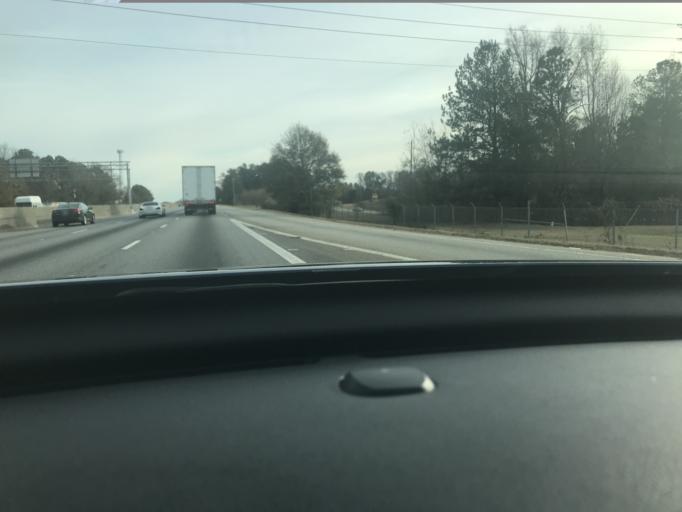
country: US
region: Georgia
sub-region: Rockdale County
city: Lakeview Estates
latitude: 33.6819
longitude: -84.0631
